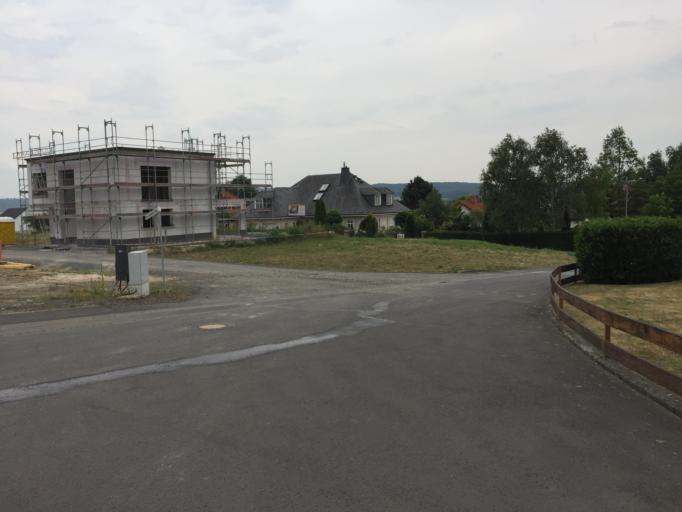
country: DE
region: Hesse
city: Staufenberg
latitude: 50.6639
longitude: 8.7352
